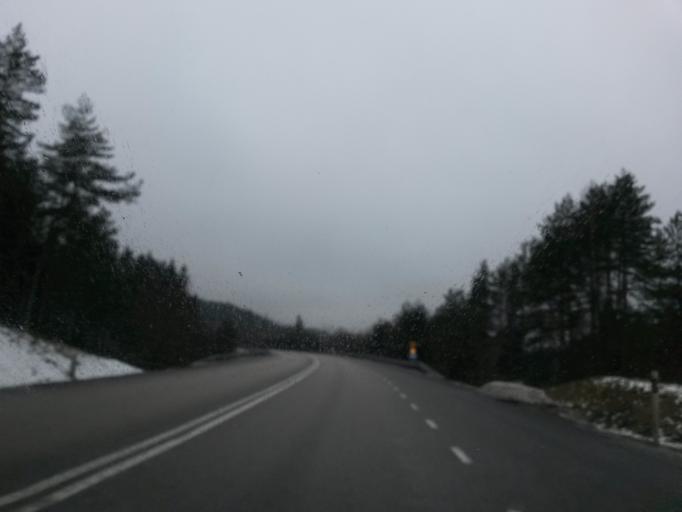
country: SE
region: Vaestra Goetaland
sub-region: Marks Kommun
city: Fritsla
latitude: 57.5719
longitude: 12.8386
